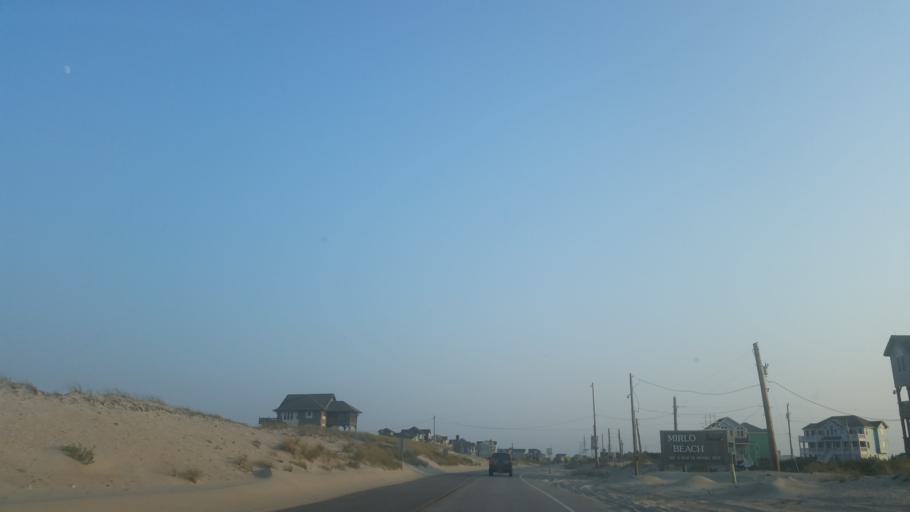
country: US
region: North Carolina
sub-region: Dare County
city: Wanchese
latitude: 35.6077
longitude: -75.4657
